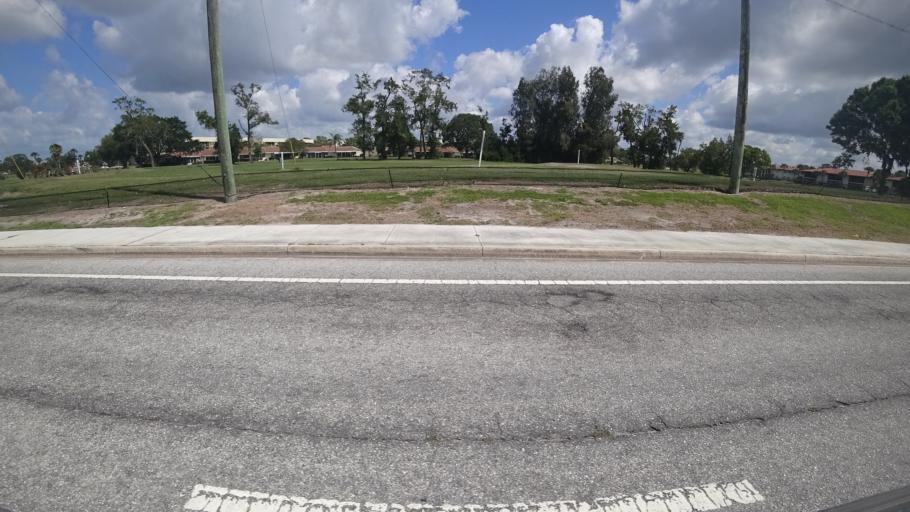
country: US
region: Florida
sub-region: Manatee County
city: Bayshore Gardens
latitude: 27.4294
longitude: -82.6024
